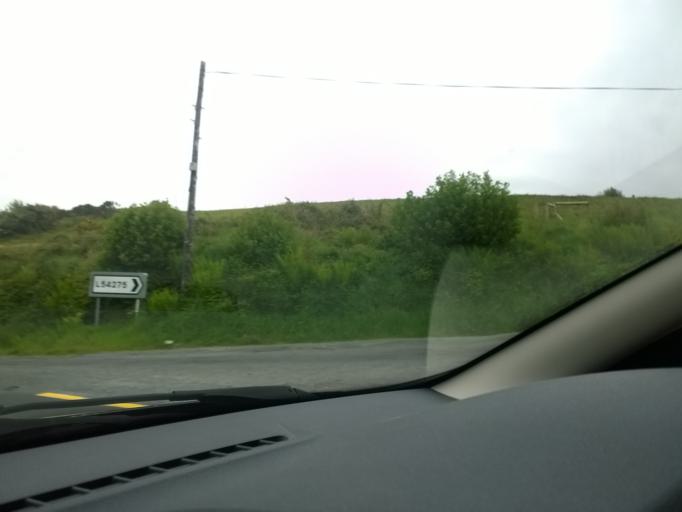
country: IE
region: Connaught
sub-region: Maigh Eo
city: Westport
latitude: 53.8572
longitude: -9.5448
